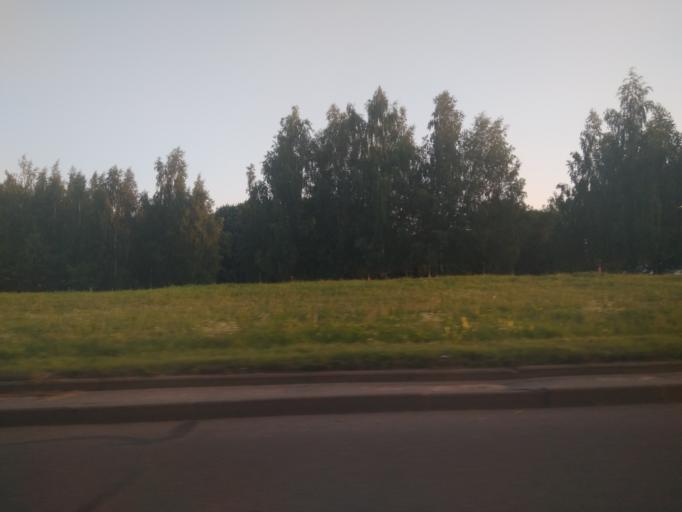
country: BY
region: Minsk
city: Novoye Medvezhino
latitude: 53.9293
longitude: 27.4808
